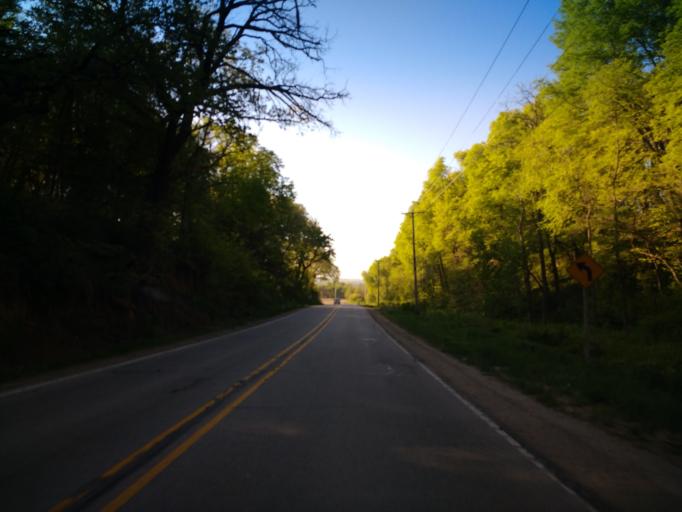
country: US
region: Iowa
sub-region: Harrison County
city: Missouri Valley
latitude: 41.4195
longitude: -95.8496
